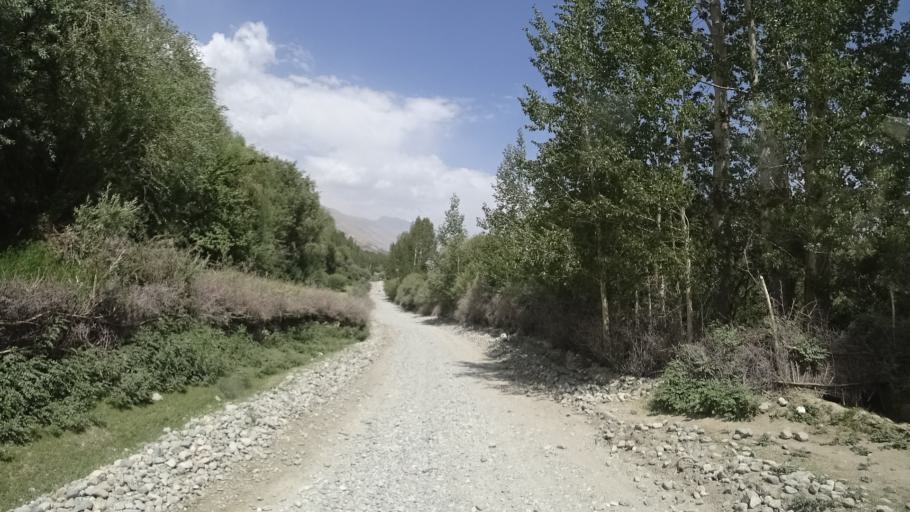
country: AF
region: Badakhshan
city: Khandud
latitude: 36.9368
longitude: 72.2179
